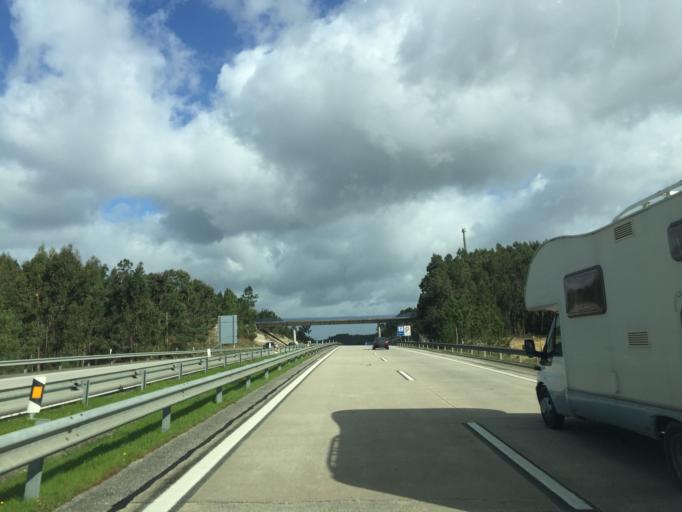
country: PT
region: Lisbon
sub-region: Torres Vedras
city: A dos Cunhados
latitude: 39.1420
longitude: -9.2470
